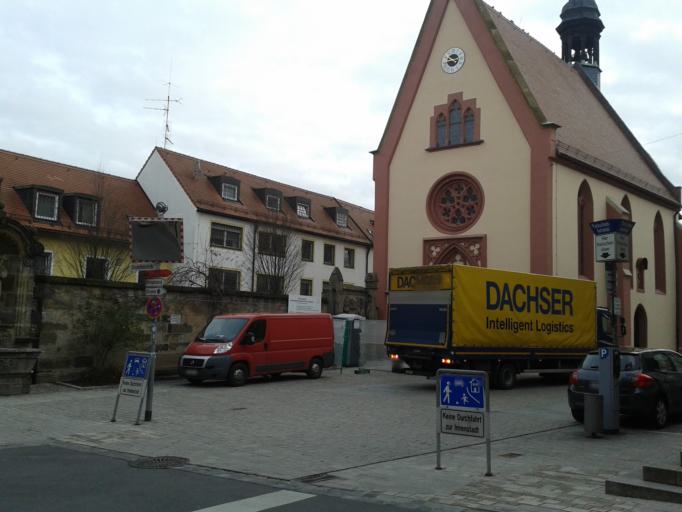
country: DE
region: Bavaria
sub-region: Upper Franconia
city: Bamberg
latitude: 49.8929
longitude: 10.8825
